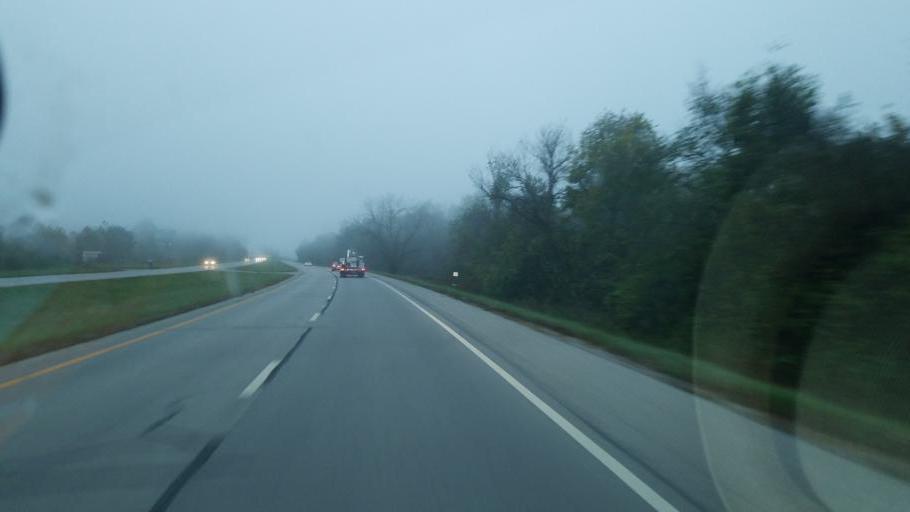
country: US
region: Ohio
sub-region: Pike County
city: Piketon
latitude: 38.9999
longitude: -83.0266
